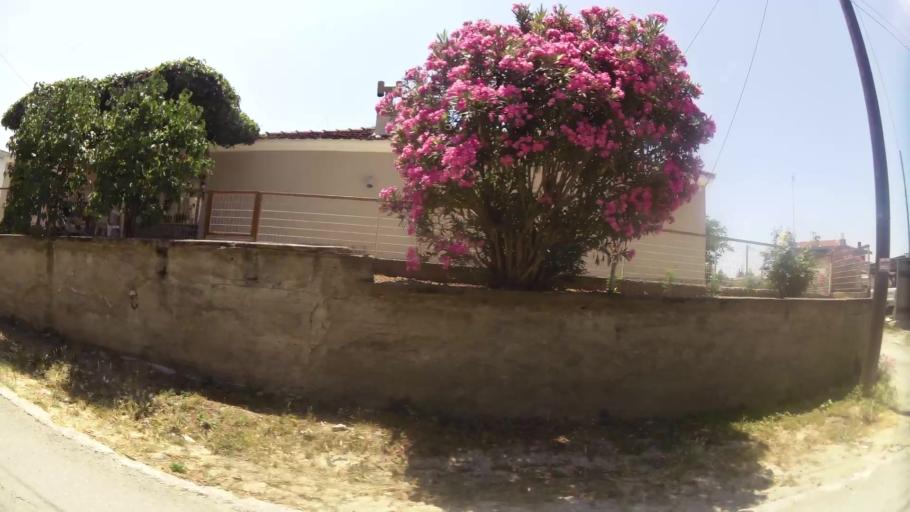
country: GR
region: Central Macedonia
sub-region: Nomos Thessalonikis
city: Epanomi
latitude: 40.4273
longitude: 22.9334
